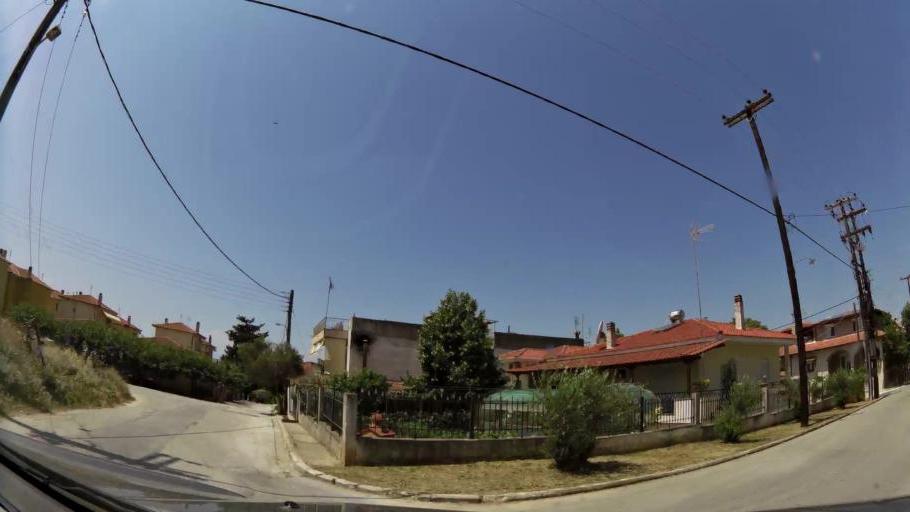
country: GR
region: Central Macedonia
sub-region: Nomos Thessalonikis
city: Nea Michaniona
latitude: 40.4747
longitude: 22.8710
